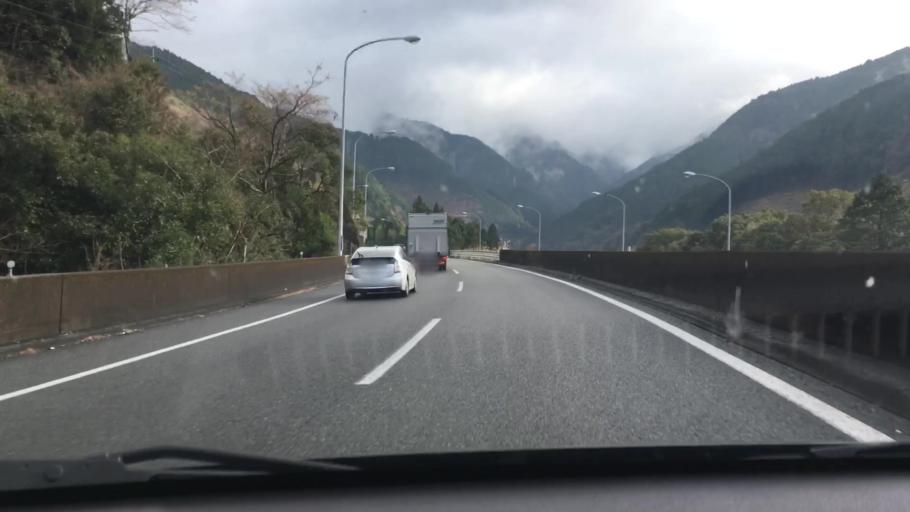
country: JP
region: Kumamoto
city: Yatsushiro
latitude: 32.4021
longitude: 130.6983
